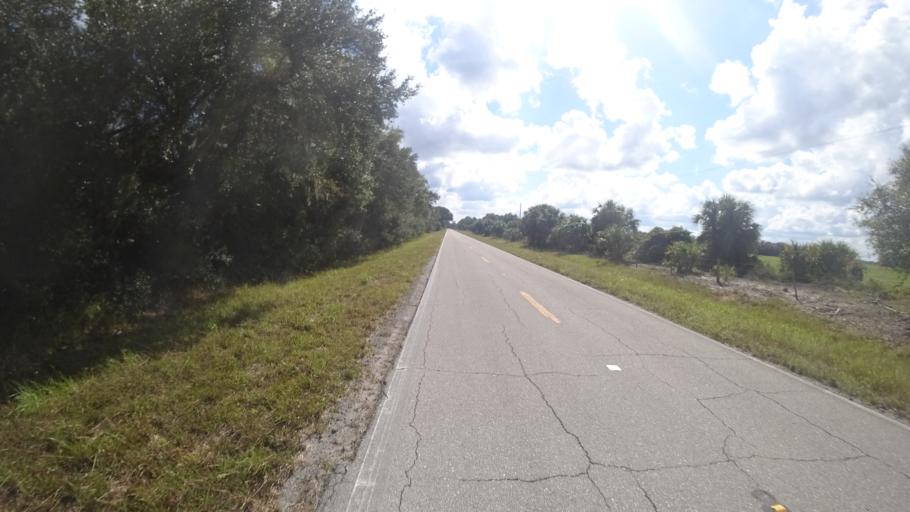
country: US
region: Florida
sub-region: Sarasota County
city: North Port
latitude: 27.2253
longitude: -82.1220
